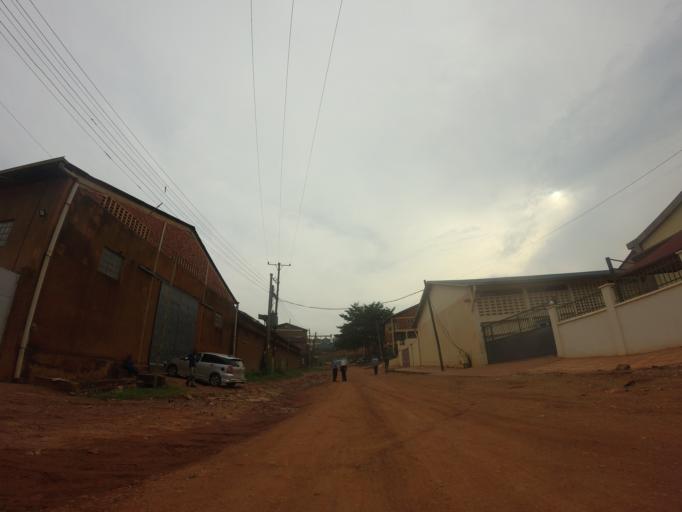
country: UG
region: Central Region
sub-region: Wakiso District
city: Kireka
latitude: 0.3379
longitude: 32.6212
